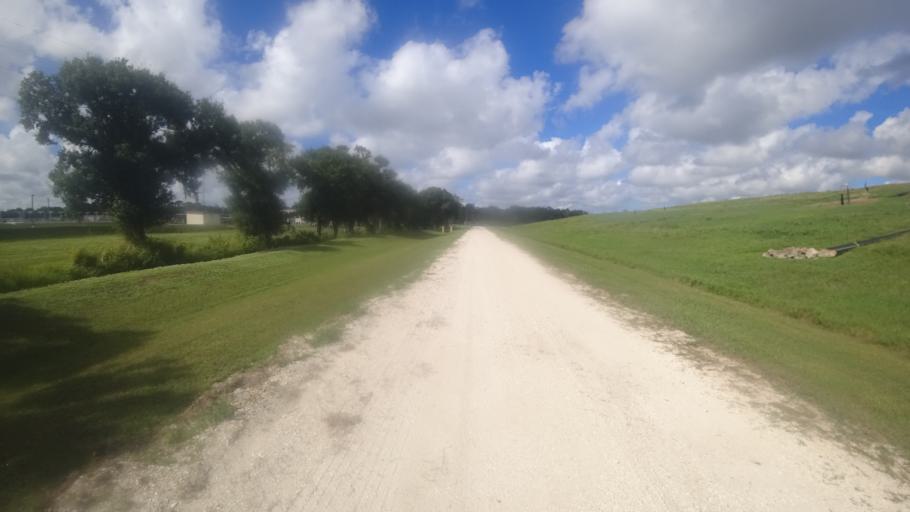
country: US
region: Florida
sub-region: Manatee County
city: Samoset
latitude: 27.4690
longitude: -82.4498
